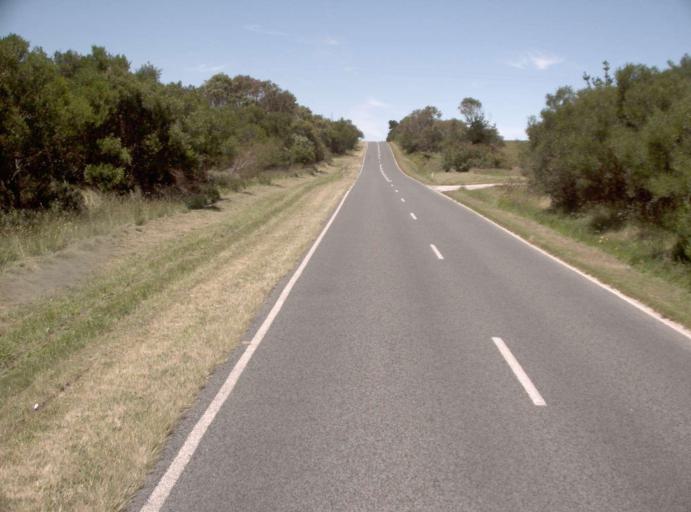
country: AU
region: Victoria
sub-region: Bass Coast
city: North Wonthaggi
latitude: -38.7625
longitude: 146.1516
